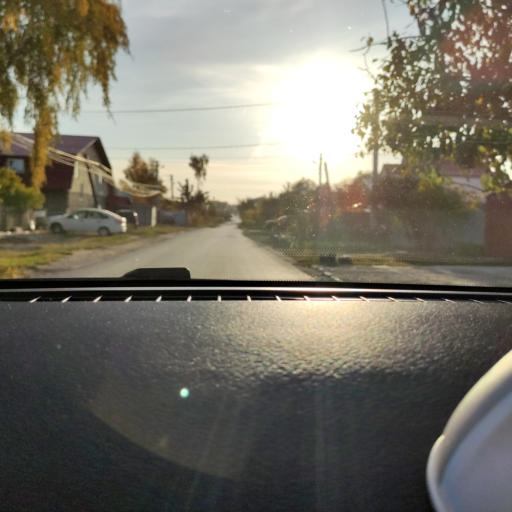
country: RU
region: Samara
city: Samara
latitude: 53.2322
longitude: 50.2331
